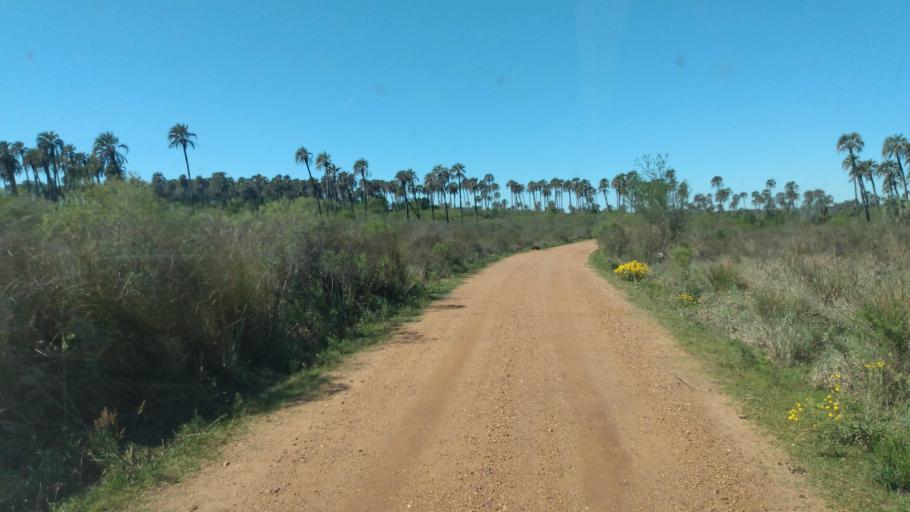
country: AR
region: Entre Rios
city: Ubajay
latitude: -31.8835
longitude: -58.2368
